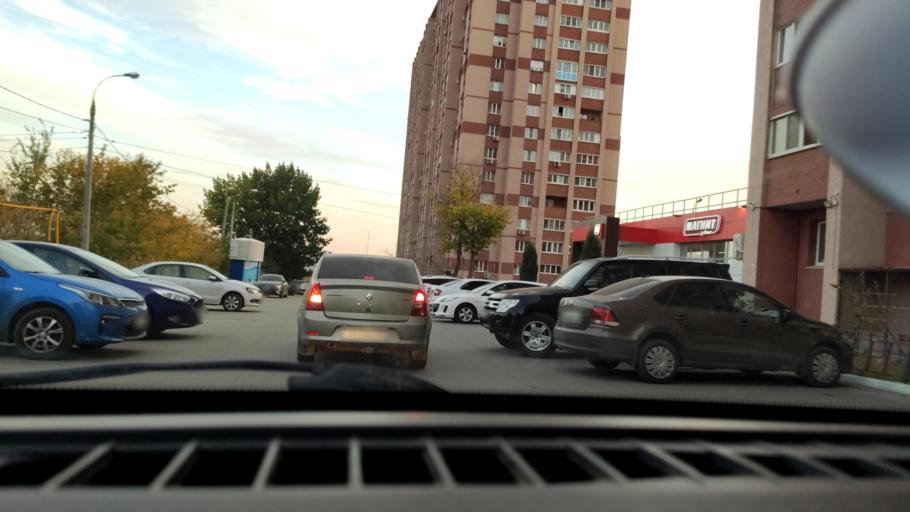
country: RU
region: Samara
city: Samara
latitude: 53.2082
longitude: 50.2082
